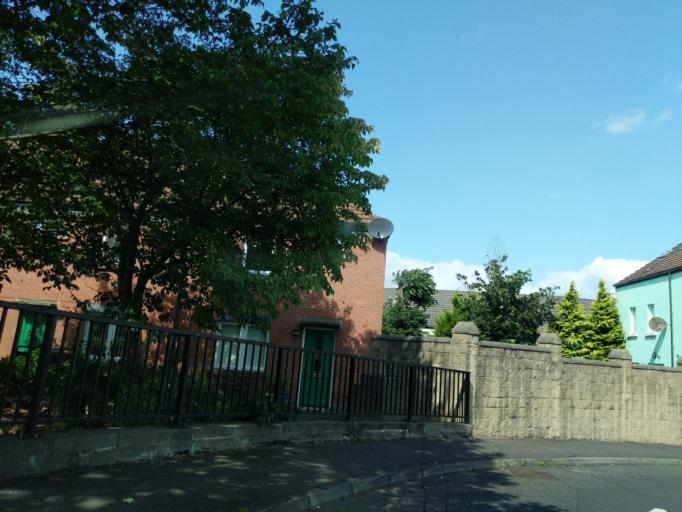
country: GB
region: Scotland
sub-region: Edinburgh
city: Currie
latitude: 55.9151
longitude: -3.2898
